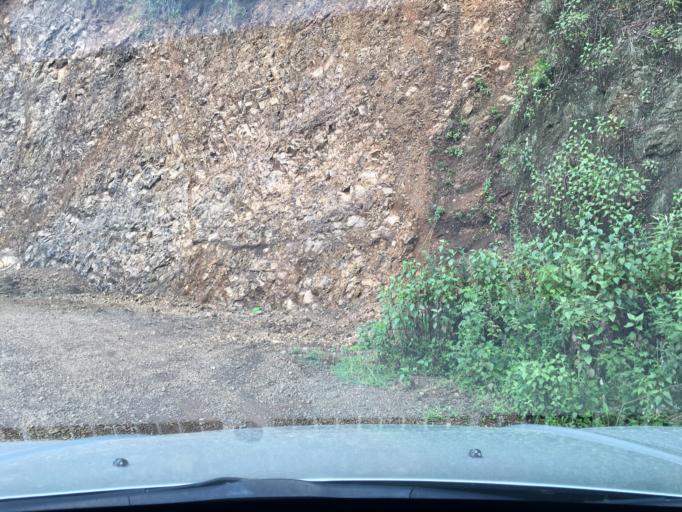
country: CN
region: Guizhou Sheng
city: Liupanshui
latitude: 25.9085
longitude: 105.1149
